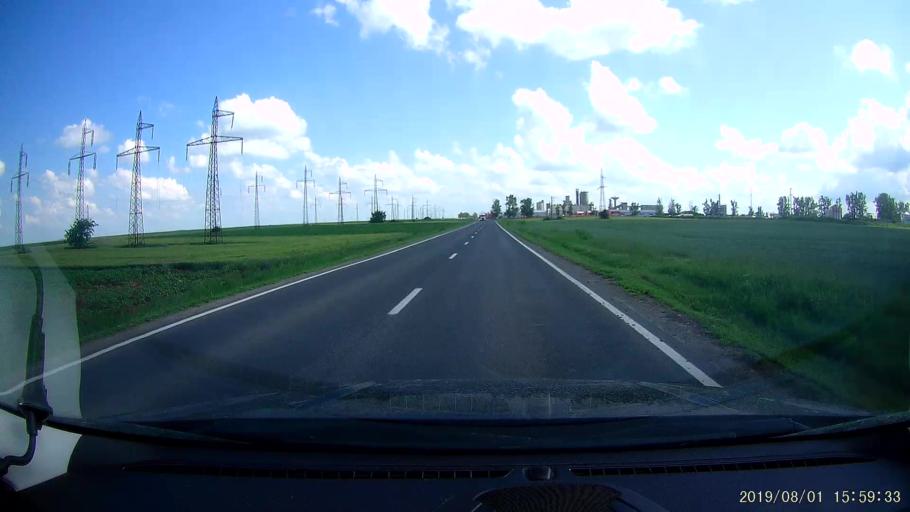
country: RO
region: Ialomita
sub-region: Comuna Slobozia
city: Slobozia
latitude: 44.5463
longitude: 27.3840
